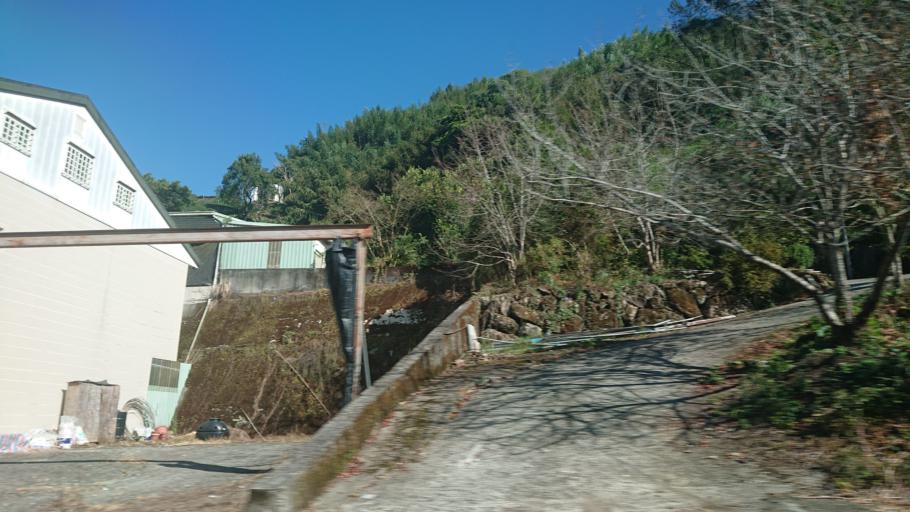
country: TW
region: Taiwan
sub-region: Chiayi
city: Jiayi Shi
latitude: 23.4711
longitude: 120.7078
